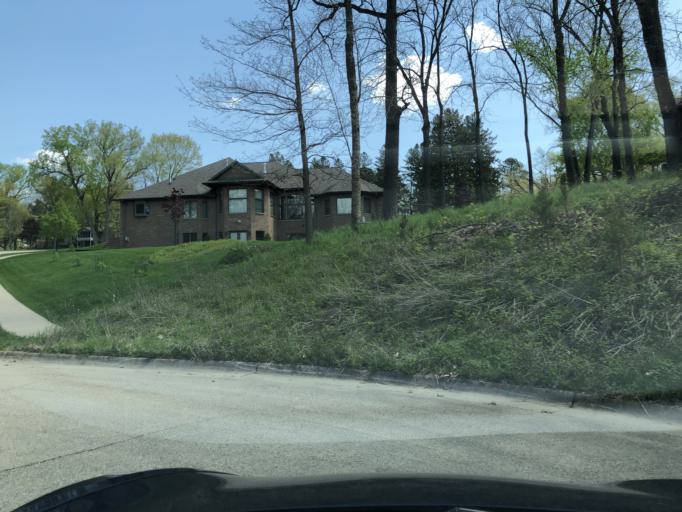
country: US
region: Iowa
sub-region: Dubuque County
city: Dubuque
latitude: 42.4763
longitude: -90.6639
